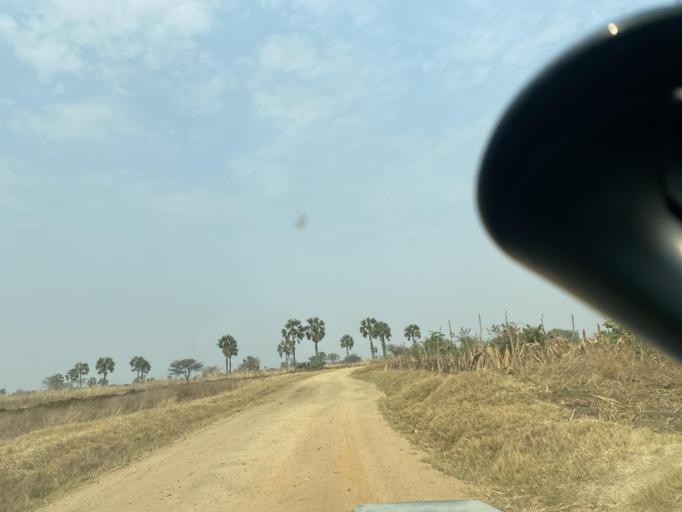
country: ZM
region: Lusaka
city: Kafue
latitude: -15.6504
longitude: 28.0660
